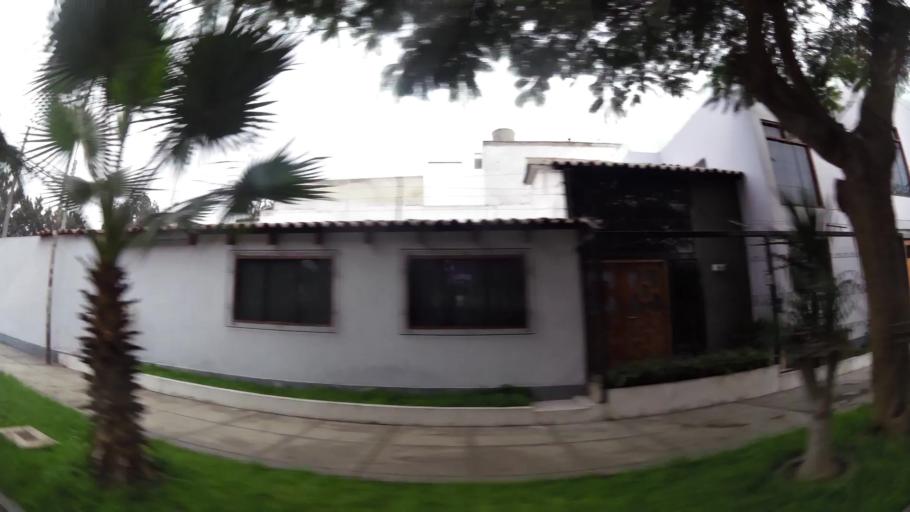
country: PE
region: Lima
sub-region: Lima
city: La Molina
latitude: -12.0972
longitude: -76.9453
